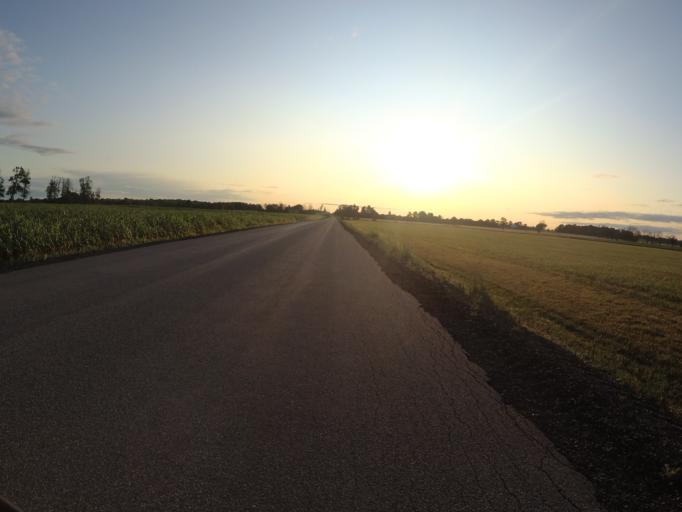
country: CA
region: Ontario
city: Ottawa
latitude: 45.1350
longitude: -75.4705
